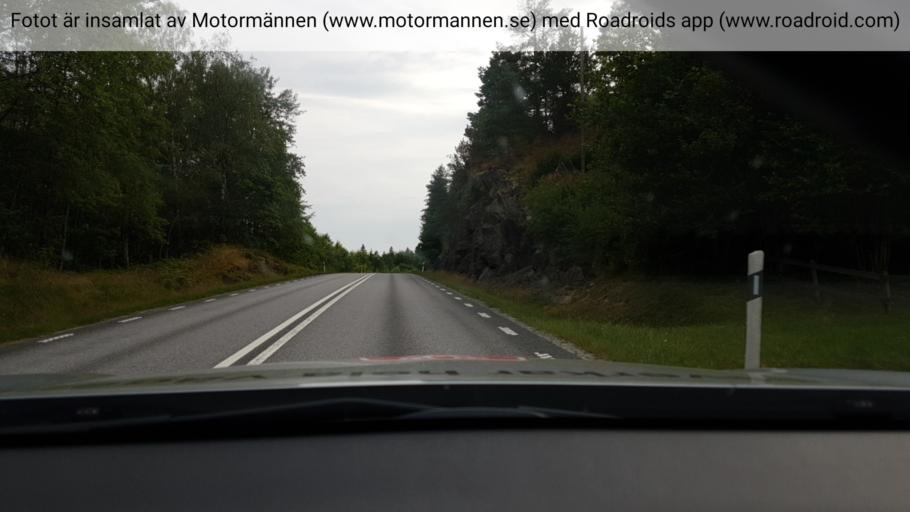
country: SE
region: Vaestra Goetaland
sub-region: Uddevalla Kommun
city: Uddevalla
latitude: 58.4136
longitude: 12.0154
